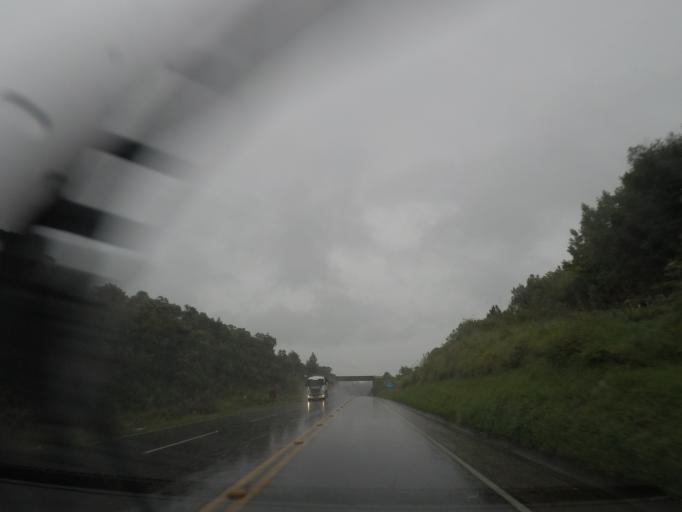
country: BR
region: Parana
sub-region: Almirante Tamandare
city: Almirante Tamandare
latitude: -25.3599
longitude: -49.3134
